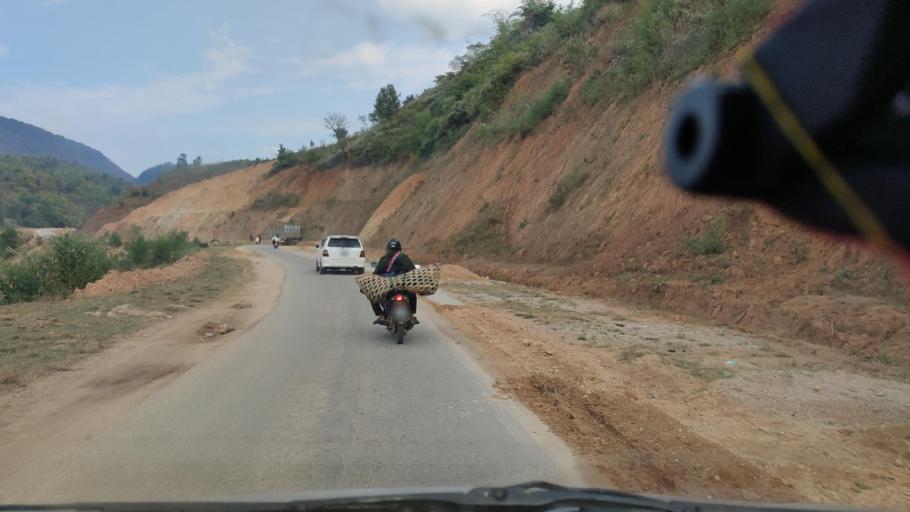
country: CN
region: Yunnan
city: Nayun
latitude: 21.7579
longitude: 99.4832
